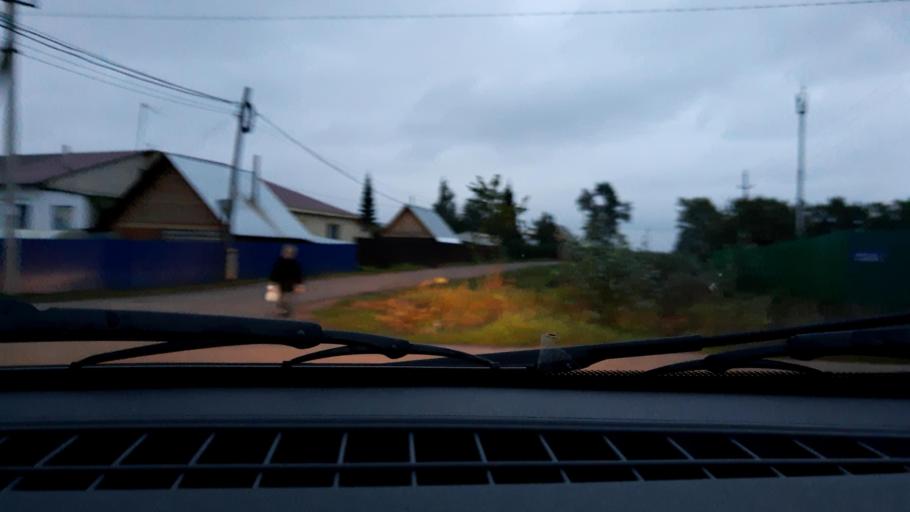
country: RU
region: Bashkortostan
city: Mikhaylovka
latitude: 54.8622
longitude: 55.8093
